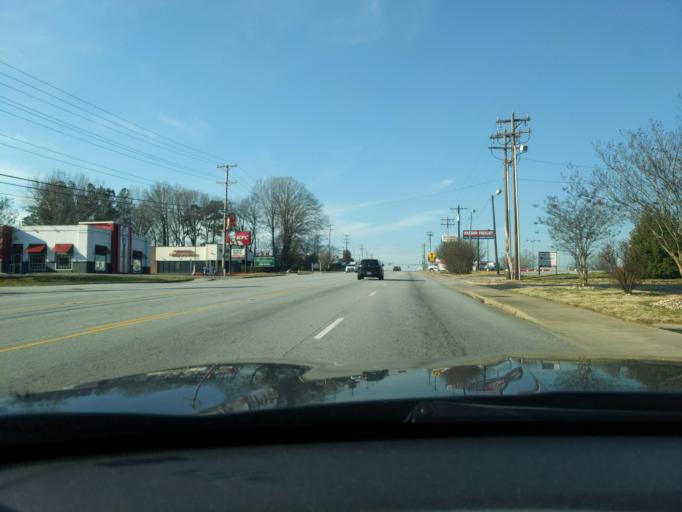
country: US
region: South Carolina
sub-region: Greenwood County
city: Greenwood
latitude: 34.2132
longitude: -82.1748
